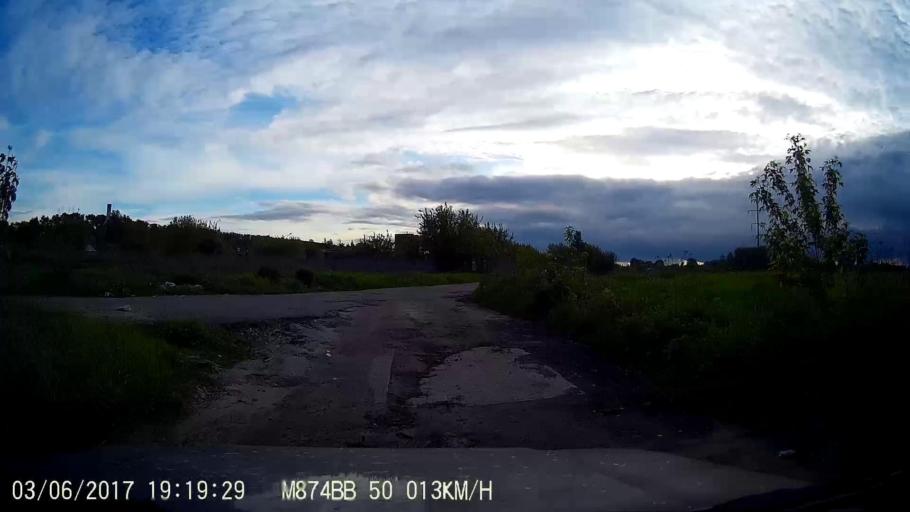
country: RU
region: Moskovskaya
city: Sychevo
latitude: 55.0671
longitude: 38.7326
